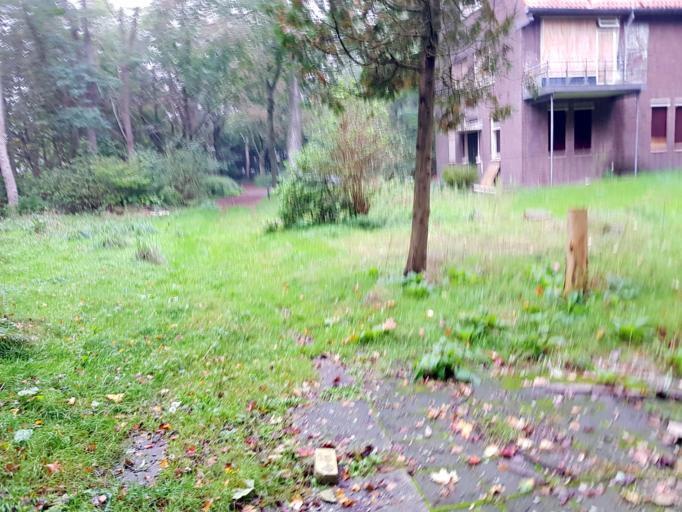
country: NL
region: Utrecht
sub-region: Gemeente Utrechtse Heuvelrug
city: Maarsbergen
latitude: 52.0382
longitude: 5.4213
